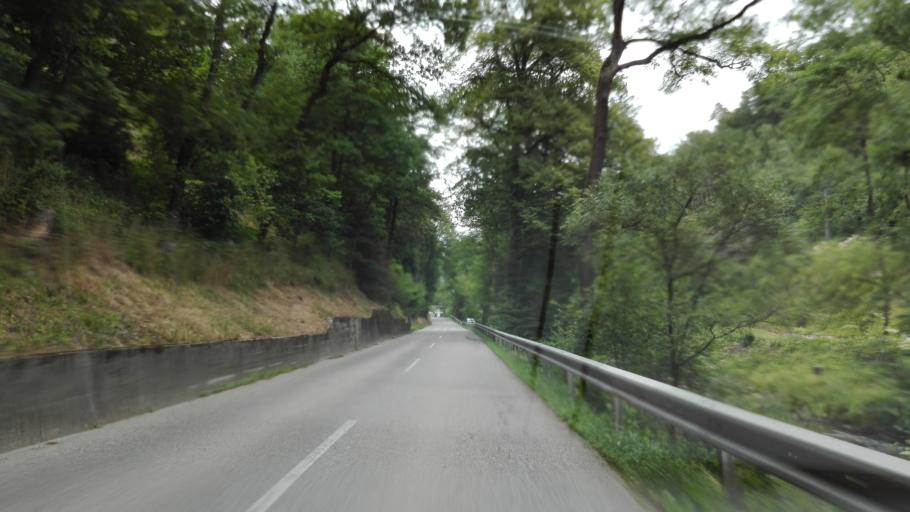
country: AT
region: Upper Austria
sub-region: Politischer Bezirk Urfahr-Umgebung
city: Engerwitzdorf
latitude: 48.2851
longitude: 14.4622
